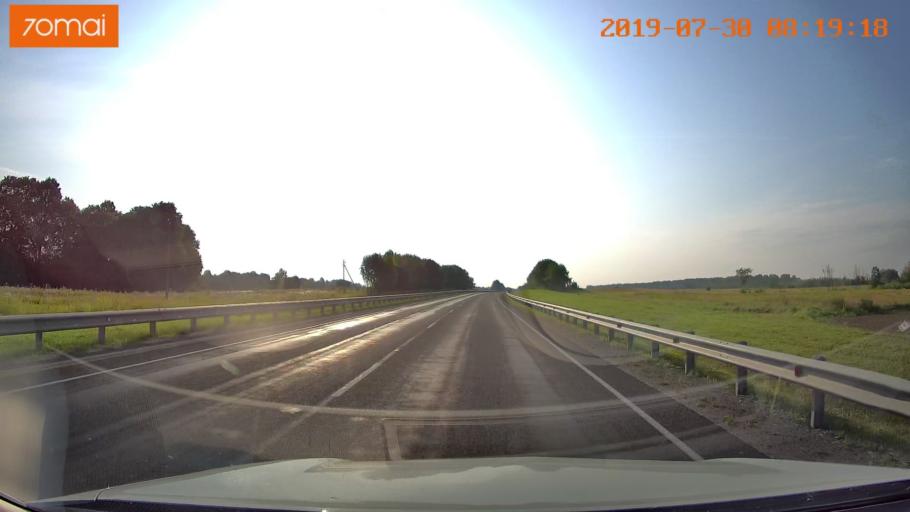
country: RU
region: Kaliningrad
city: Zheleznodorozhnyy
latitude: 54.6291
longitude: 21.4876
